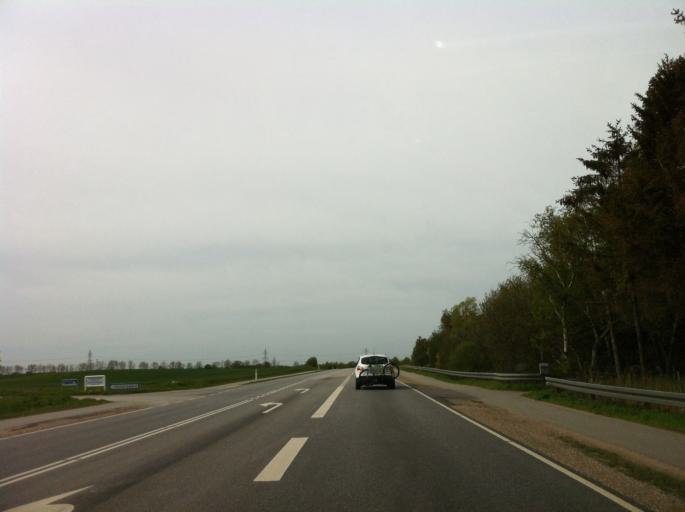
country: DK
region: Capital Region
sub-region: Frederikssund Kommune
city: Slangerup
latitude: 55.8999
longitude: 12.2299
